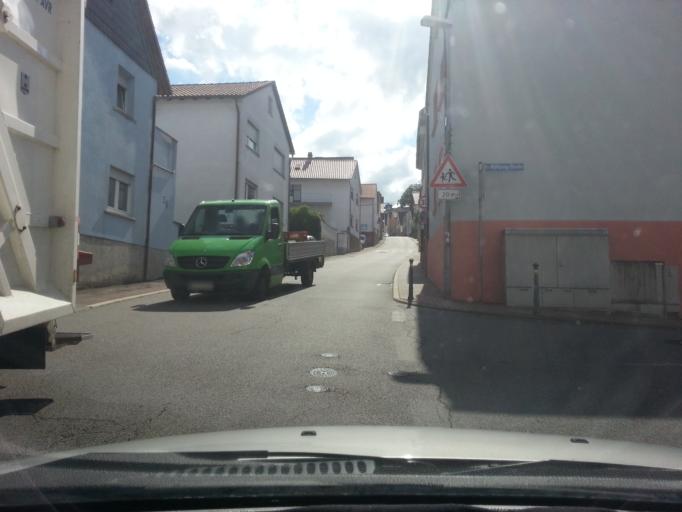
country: DE
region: Baden-Wuerttemberg
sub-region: Karlsruhe Region
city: Malsch
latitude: 49.2554
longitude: 8.6804
